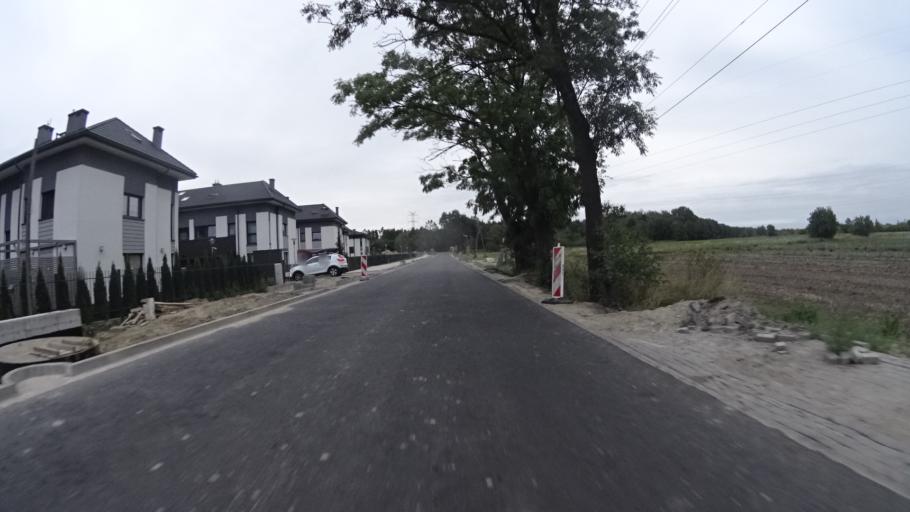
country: PL
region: Masovian Voivodeship
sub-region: Powiat warszawski zachodni
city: Stare Babice
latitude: 52.2689
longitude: 20.8308
